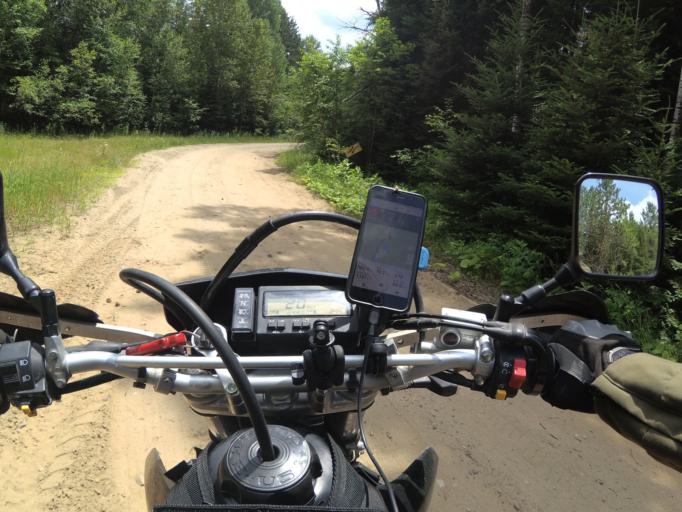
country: CA
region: Ontario
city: Bancroft
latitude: 45.0213
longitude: -77.2646
